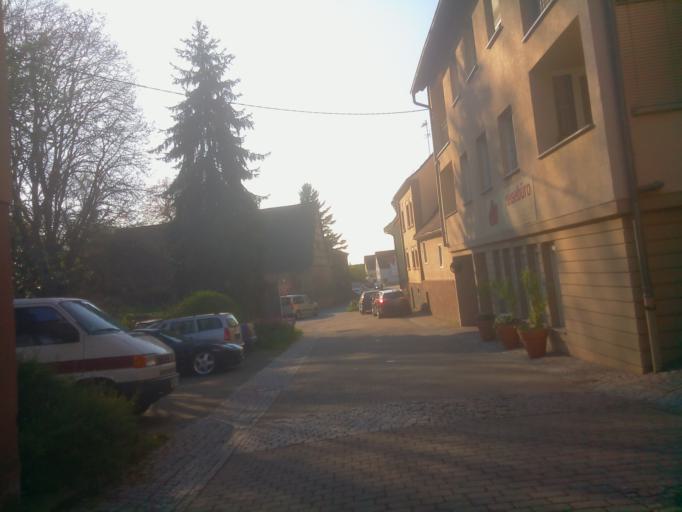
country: DE
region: Baden-Wuerttemberg
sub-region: Karlsruhe Region
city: Schriesheim
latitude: 49.5098
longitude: 8.6653
